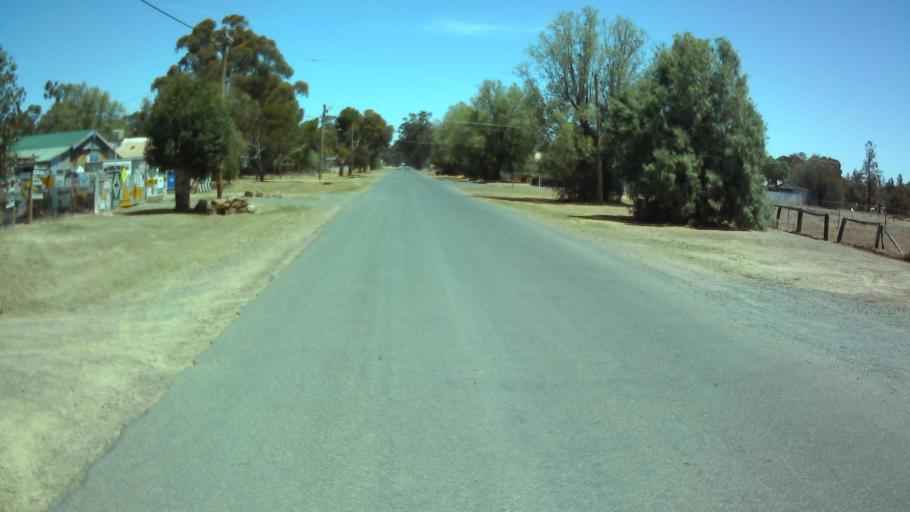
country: AU
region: New South Wales
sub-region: Weddin
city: Grenfell
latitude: -34.0114
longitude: 147.7944
